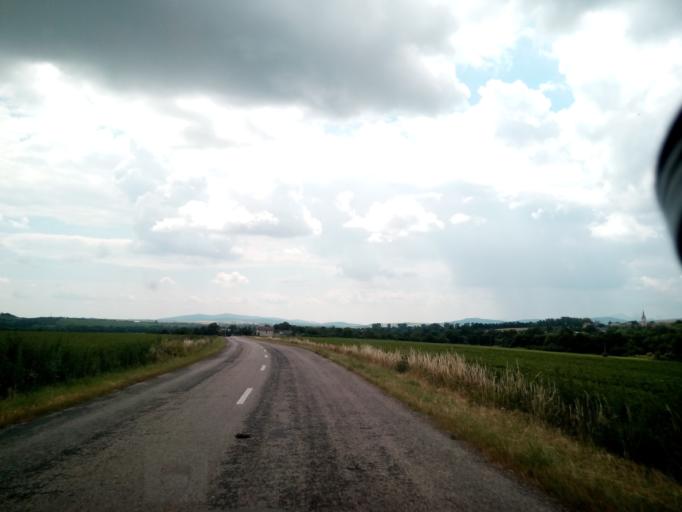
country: SK
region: Kosicky
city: Secovce
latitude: 48.6078
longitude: 21.5529
